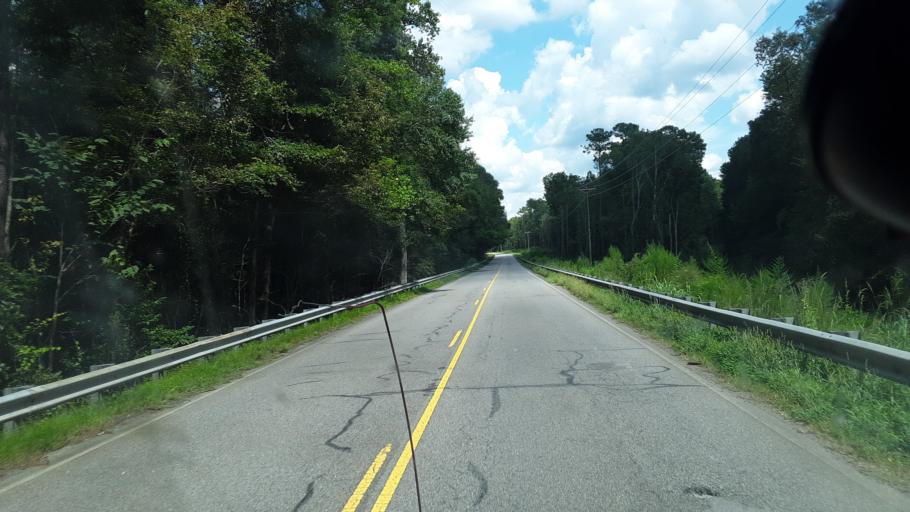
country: US
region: South Carolina
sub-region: Williamsburg County
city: Andrews
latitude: 33.5151
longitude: -79.5006
